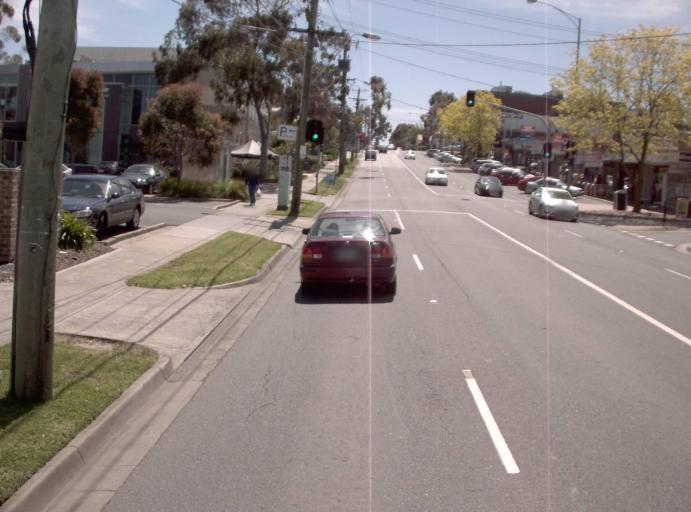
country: AU
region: Victoria
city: Burwood East
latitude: -37.8742
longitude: 145.1480
